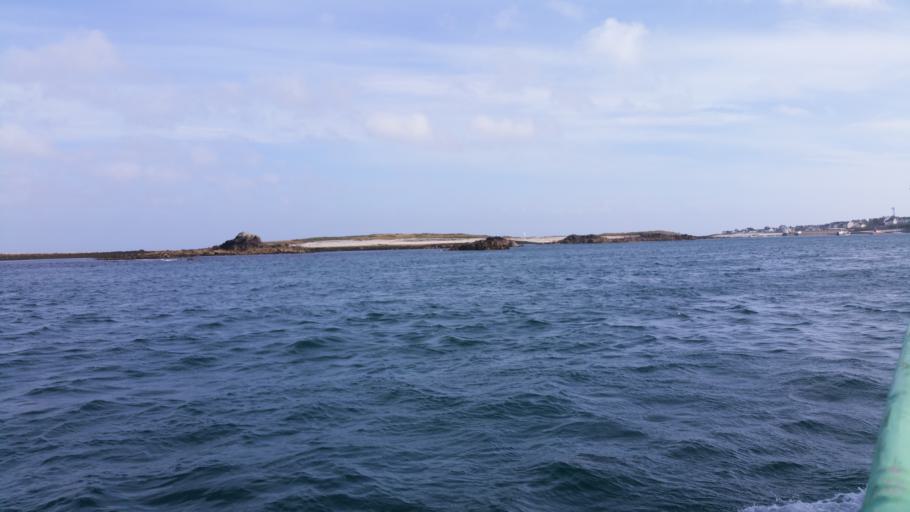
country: FR
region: Brittany
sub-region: Departement du Finistere
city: Le Conquet
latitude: 48.4082
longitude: -4.9521
